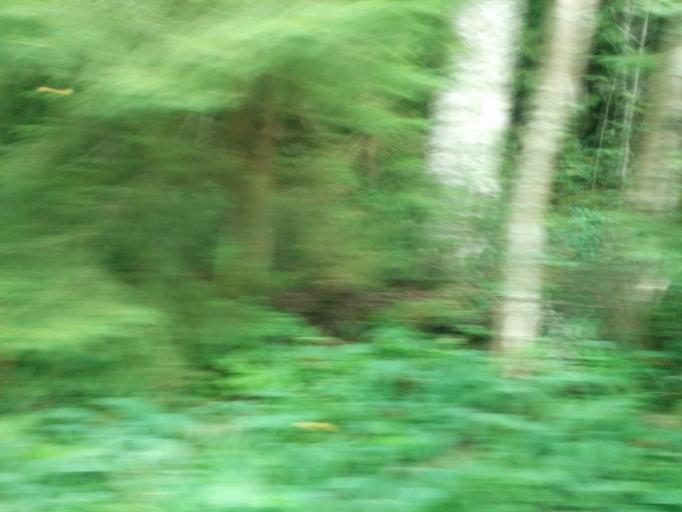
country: FI
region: Pirkanmaa
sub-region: Tampere
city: Kuhmalahti
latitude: 61.6845
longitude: 24.5612
